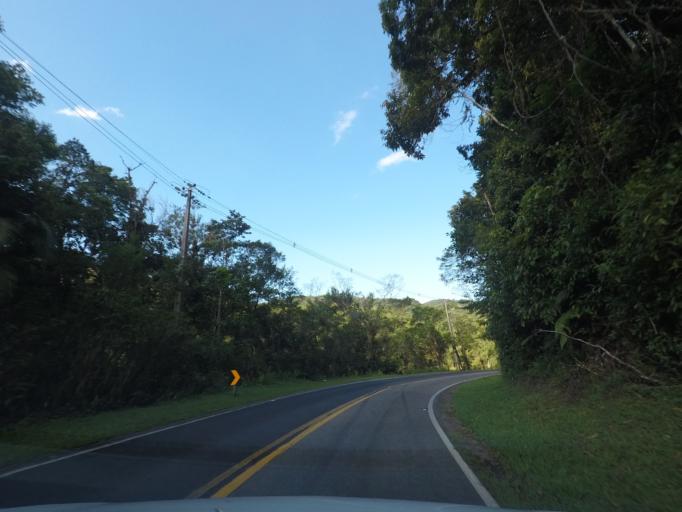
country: BR
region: Parana
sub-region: Antonina
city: Antonina
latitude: -25.4027
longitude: -48.8745
